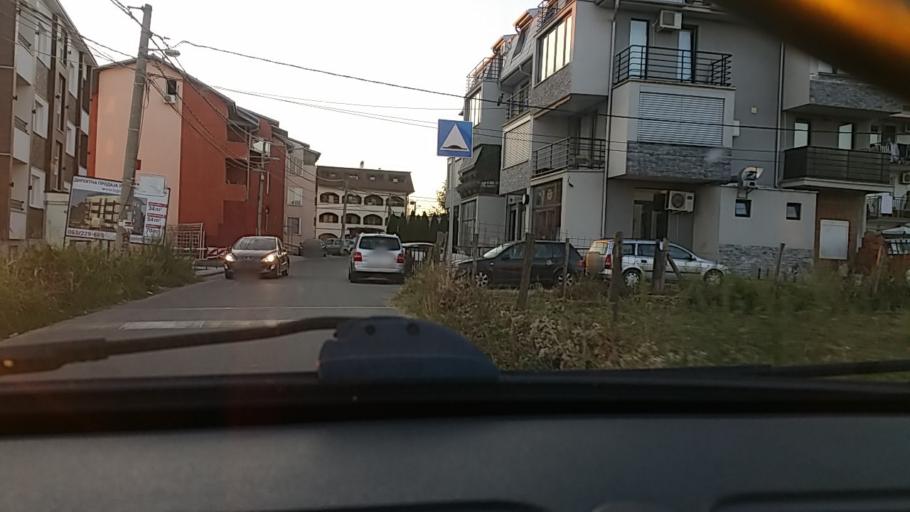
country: RS
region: Central Serbia
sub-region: Belgrade
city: Rakovica
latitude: 44.7327
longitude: 20.4684
